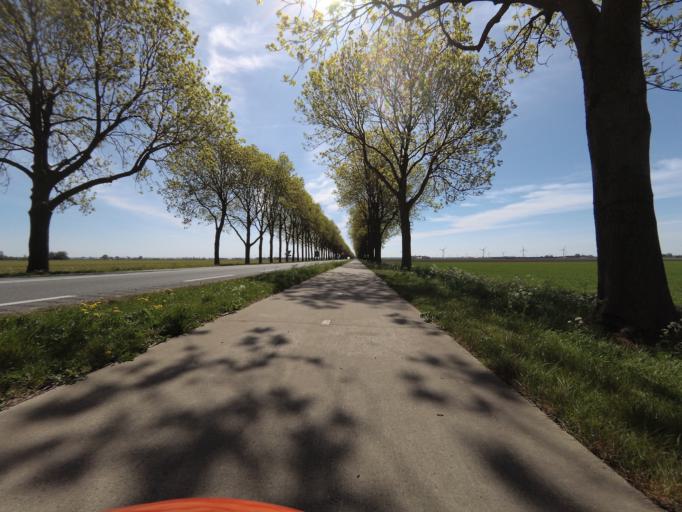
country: NL
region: Flevoland
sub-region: Gemeente Dronten
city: Biddinghuizen
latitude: 52.5062
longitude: 5.6377
